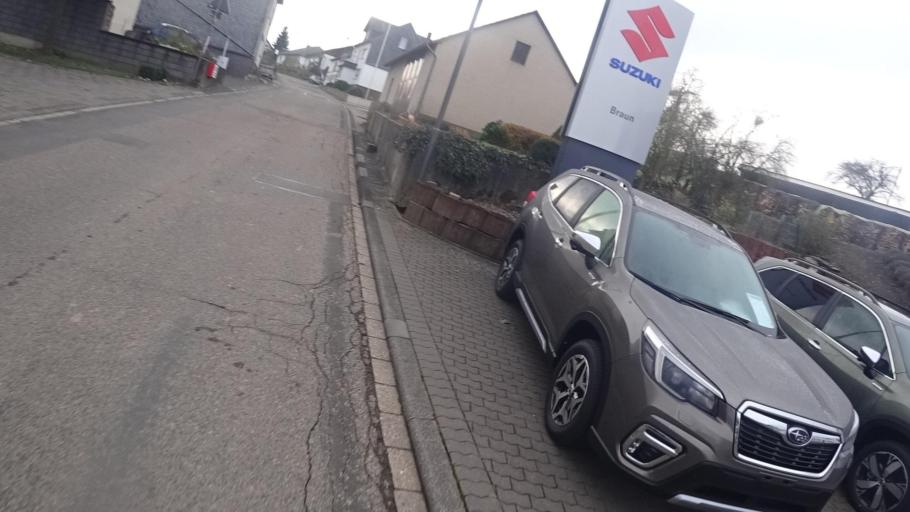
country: DE
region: Rheinland-Pfalz
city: Thorlingen
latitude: 50.1336
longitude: 7.5325
